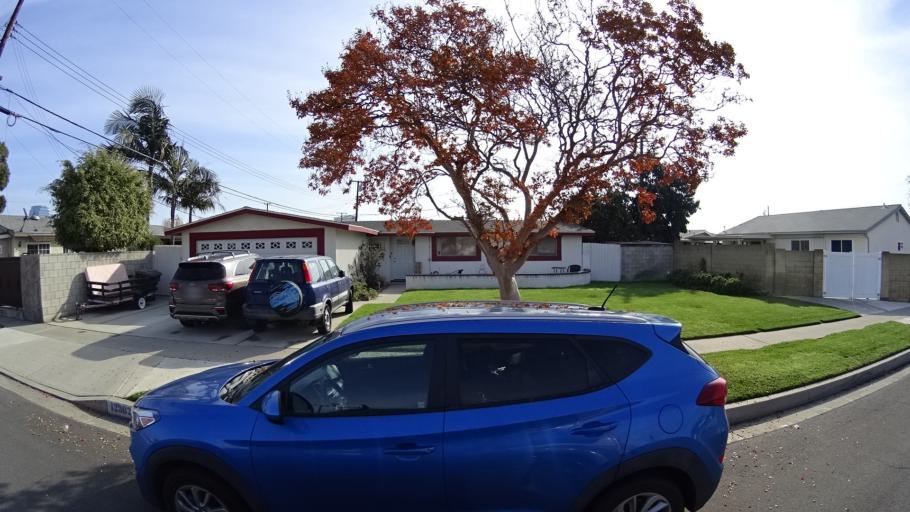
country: US
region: California
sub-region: Orange County
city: Garden Grove
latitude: 33.7844
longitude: -117.9031
